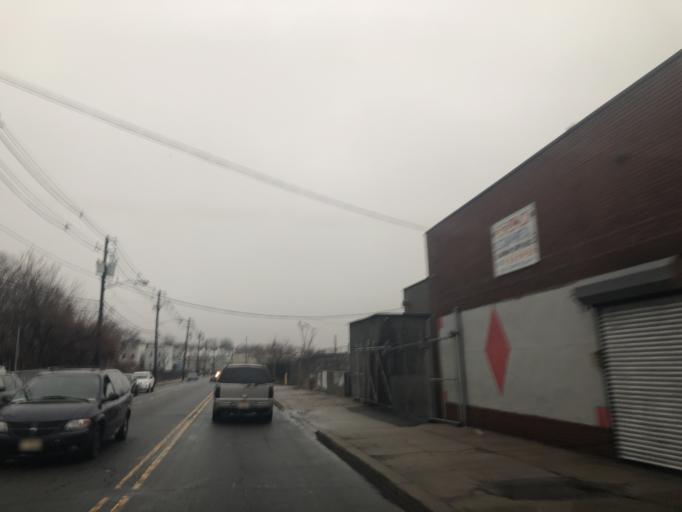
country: US
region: New Jersey
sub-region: Hudson County
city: Jersey City
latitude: 40.7067
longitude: -74.0732
